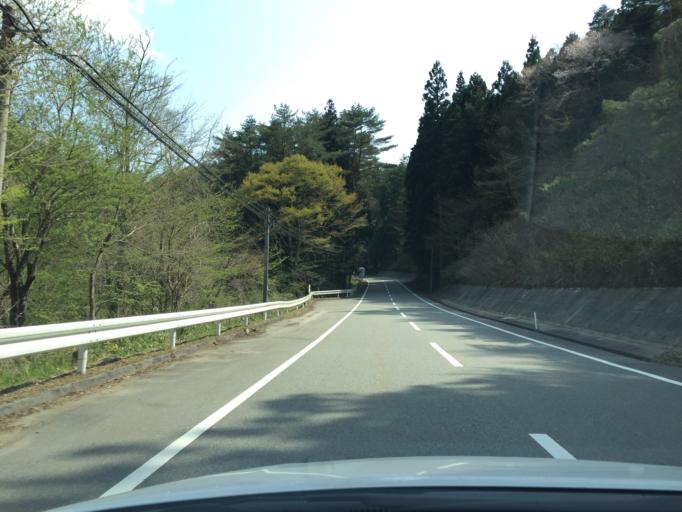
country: JP
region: Fukushima
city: Namie
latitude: 37.3036
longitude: 140.8359
